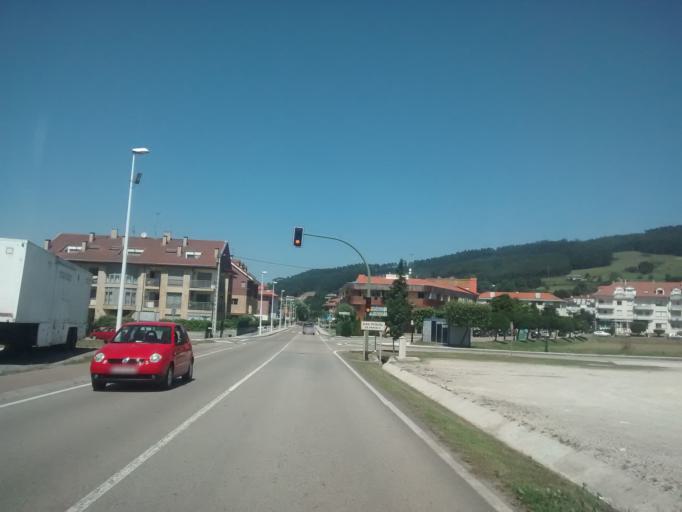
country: ES
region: Cantabria
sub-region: Provincia de Cantabria
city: San Miguel de Meruelo
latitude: 43.4519
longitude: -3.5724
